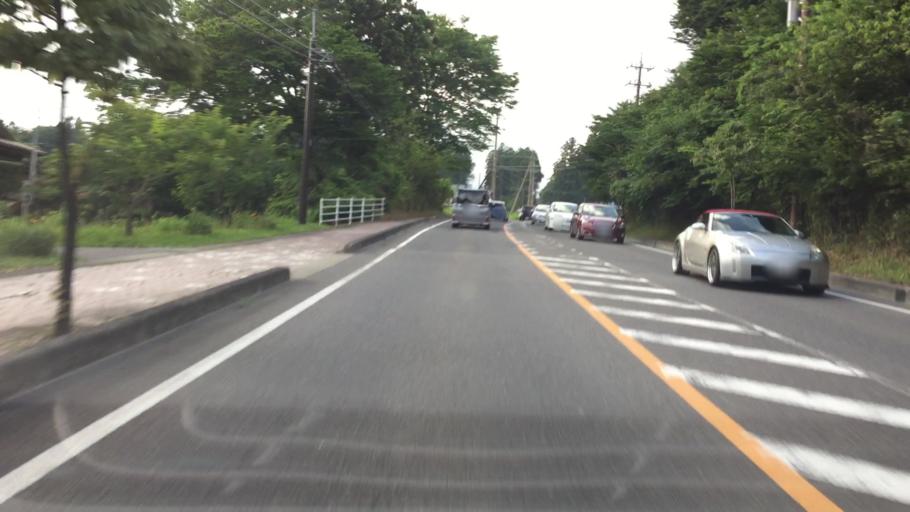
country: JP
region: Tochigi
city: Kuroiso
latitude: 37.0219
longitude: 140.0263
